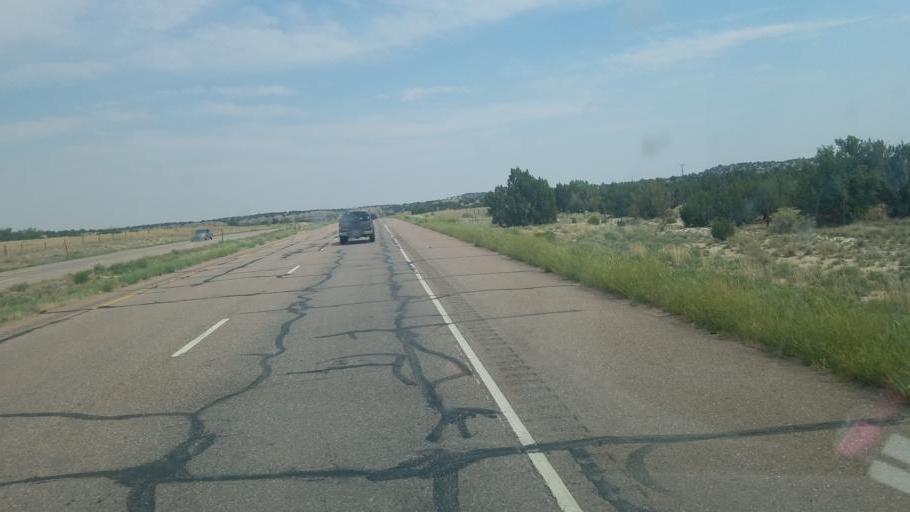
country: US
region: Colorado
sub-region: Fremont County
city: Penrose
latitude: 38.3830
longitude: -104.9568
